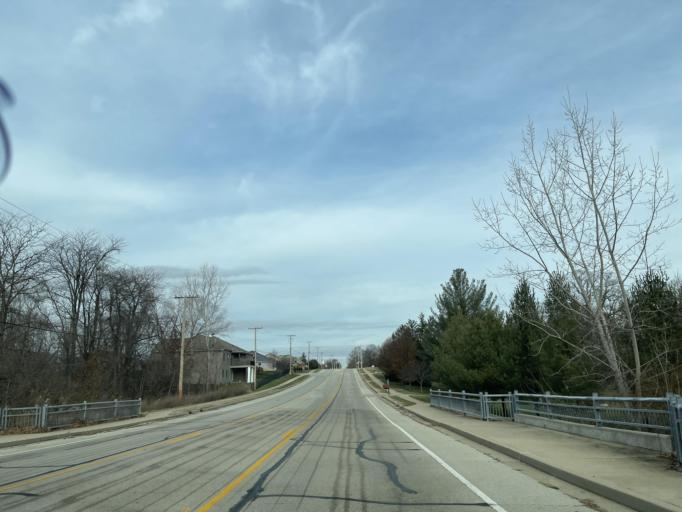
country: US
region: Illinois
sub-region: Sangamon County
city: Leland Grove
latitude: 39.7933
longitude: -89.7297
